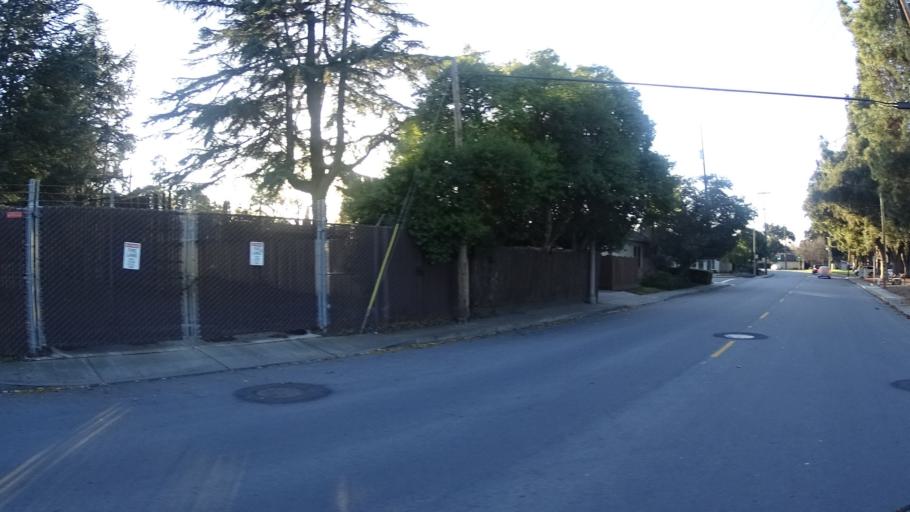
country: US
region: California
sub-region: Santa Clara County
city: Sunnyvale
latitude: 37.3810
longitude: -122.0255
